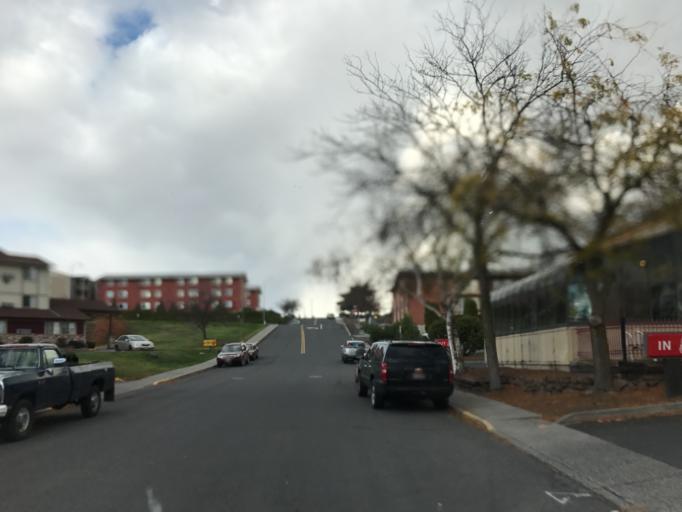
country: US
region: Idaho
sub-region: Latah County
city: Moscow
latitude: 46.7335
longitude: -117.0163
